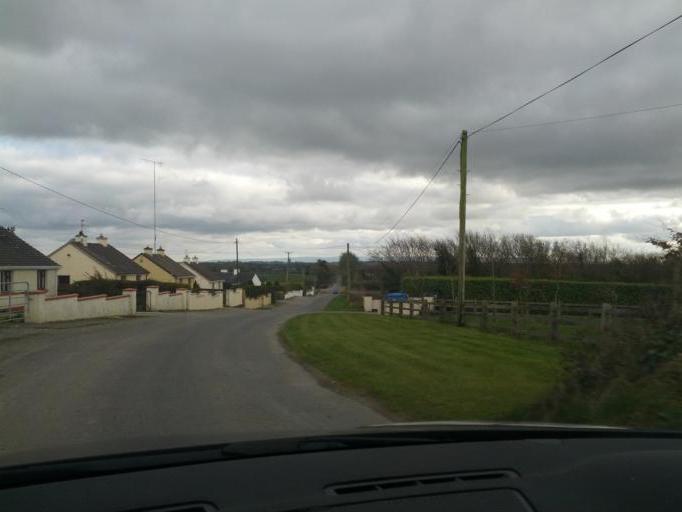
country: IE
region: Leinster
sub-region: Uibh Fhaili
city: Clara
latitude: 53.4049
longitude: -7.6218
